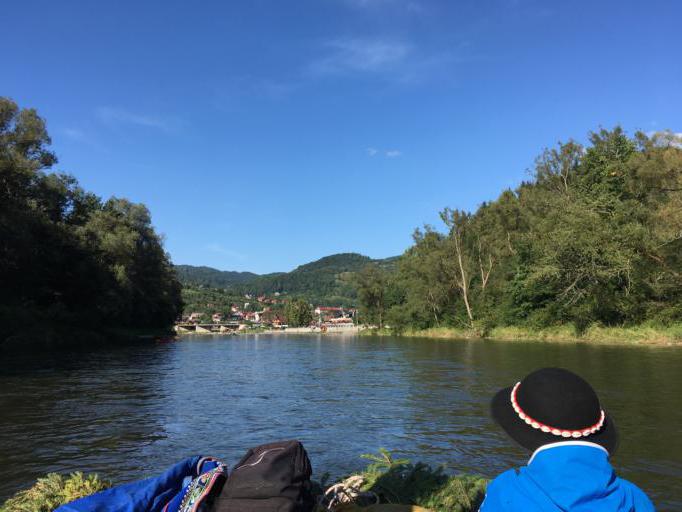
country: PL
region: Lesser Poland Voivodeship
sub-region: Powiat nowotarski
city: Szczawnica
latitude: 49.4203
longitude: 20.4566
